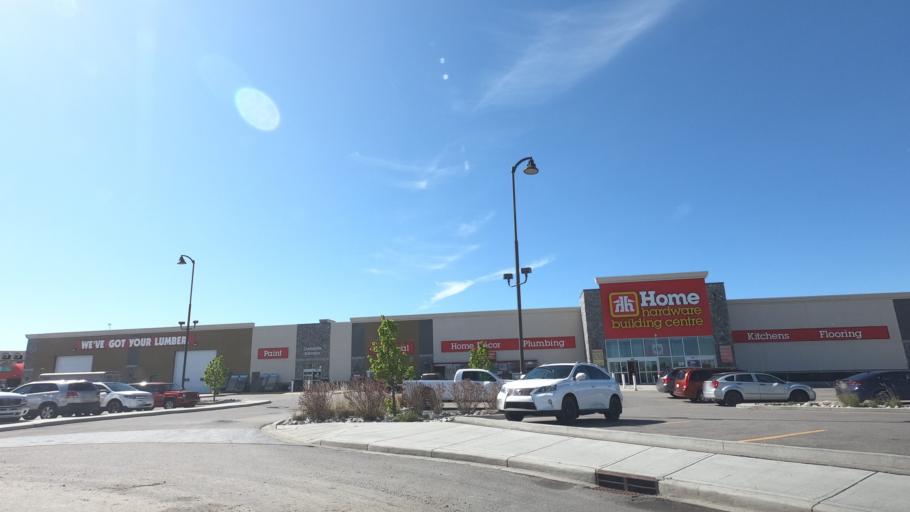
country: CA
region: Alberta
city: Airdrie
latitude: 51.2685
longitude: -113.9956
